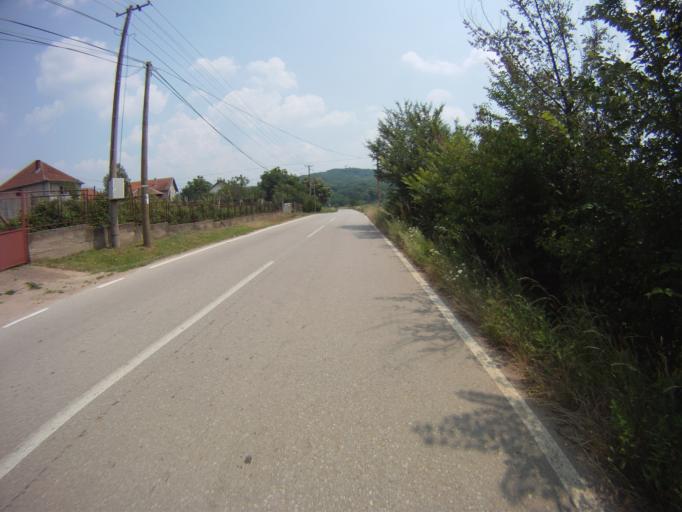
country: RS
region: Central Serbia
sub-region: Nisavski Okrug
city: Gadzin Han
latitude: 43.2061
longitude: 21.9897
